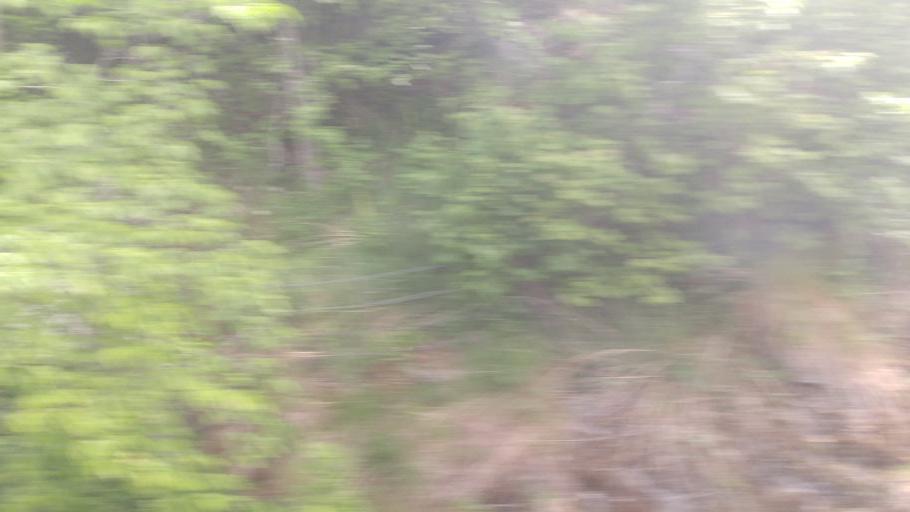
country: NO
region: Sor-Trondelag
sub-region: Melhus
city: Lundamo
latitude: 63.2190
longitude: 10.3050
